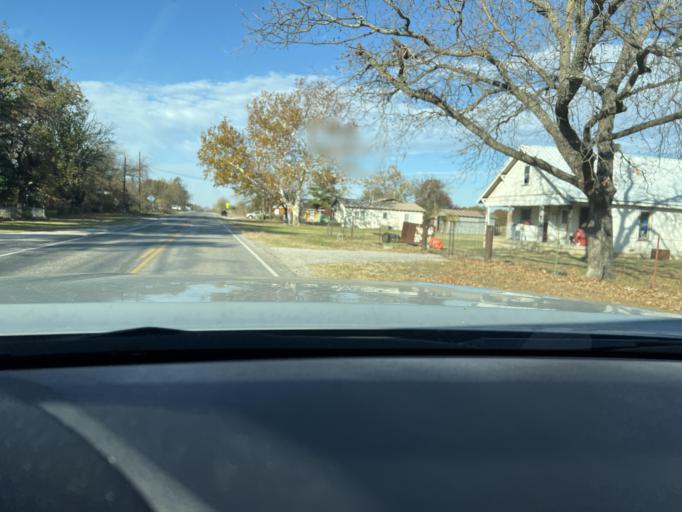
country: US
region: Texas
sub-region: Eastland County
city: Eastland
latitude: 32.4193
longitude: -98.7528
